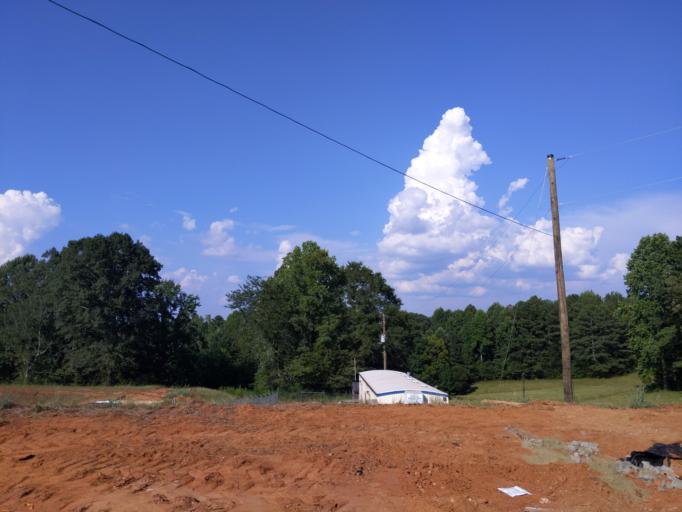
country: US
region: Georgia
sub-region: Hall County
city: Flowery Branch
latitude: 34.1466
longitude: -83.8876
